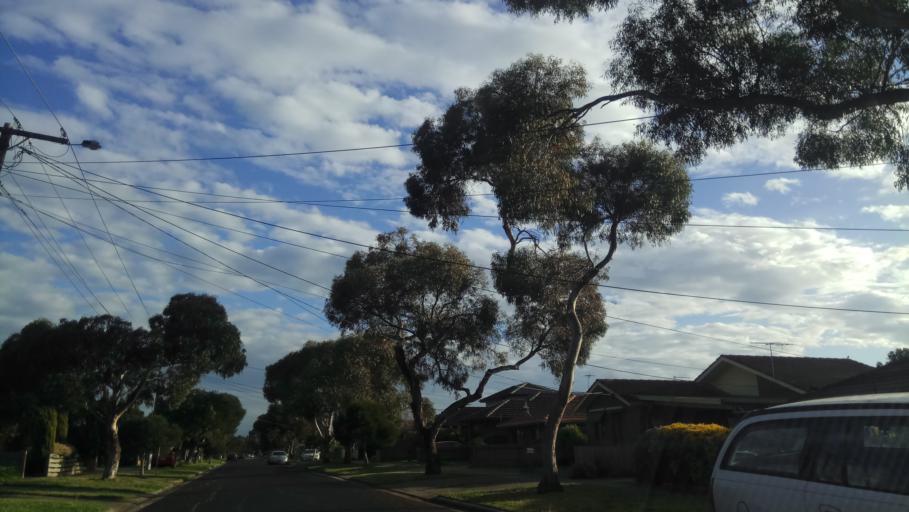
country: AU
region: Victoria
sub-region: Hobsons Bay
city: Altona Meadows
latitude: -37.8712
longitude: 144.7832
